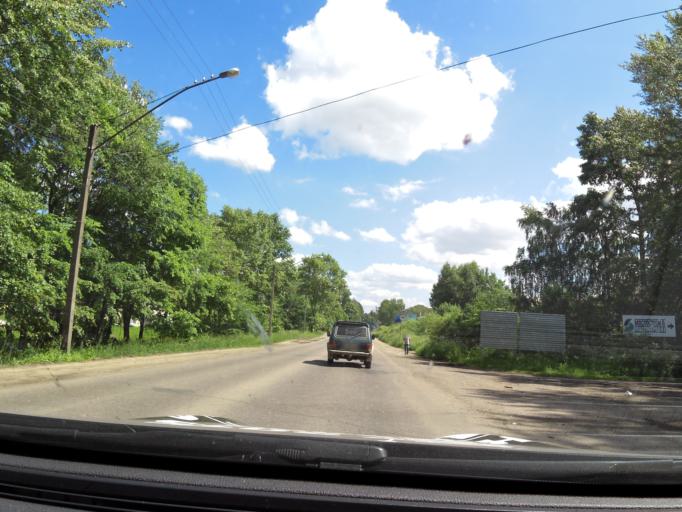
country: RU
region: Vologda
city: Vologda
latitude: 59.2384
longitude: 39.8063
